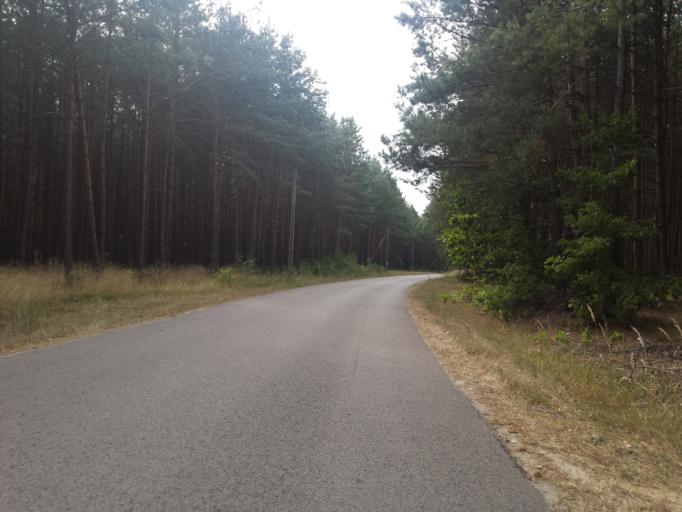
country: PL
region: Swietokrzyskie
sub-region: Powiat kielecki
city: Rakow
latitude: 50.6659
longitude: 21.1045
